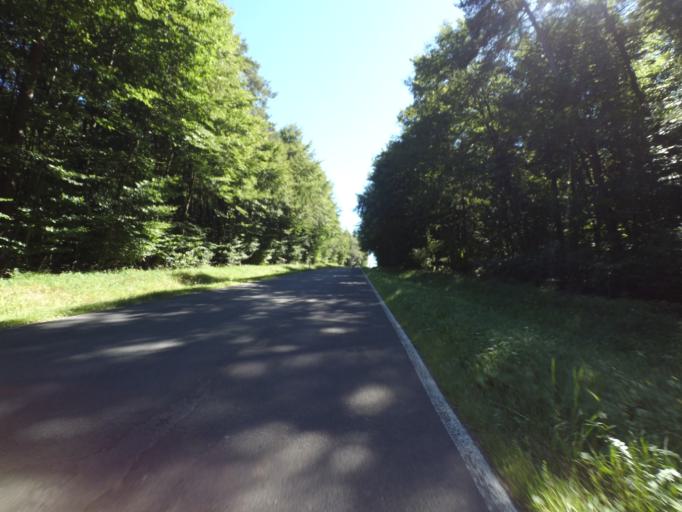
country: DE
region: Rheinland-Pfalz
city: Nohn
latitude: 50.3217
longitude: 6.7601
